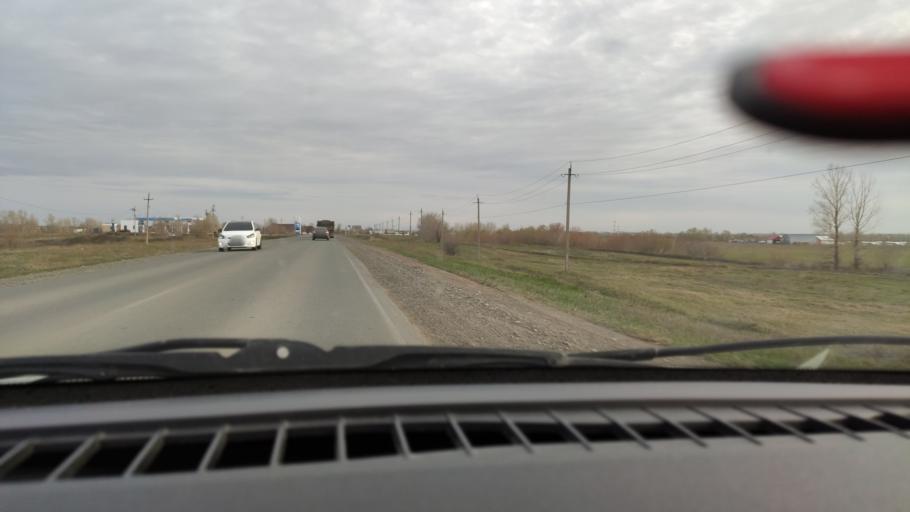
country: RU
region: Orenburg
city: Tatarskaya Kargala
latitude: 51.9074
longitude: 55.1718
